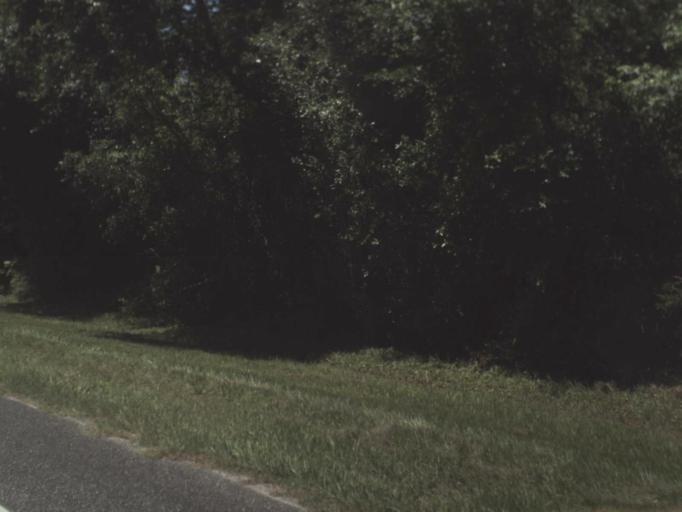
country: US
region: Florida
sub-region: Putnam County
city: Crescent City
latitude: 29.4653
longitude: -81.5260
